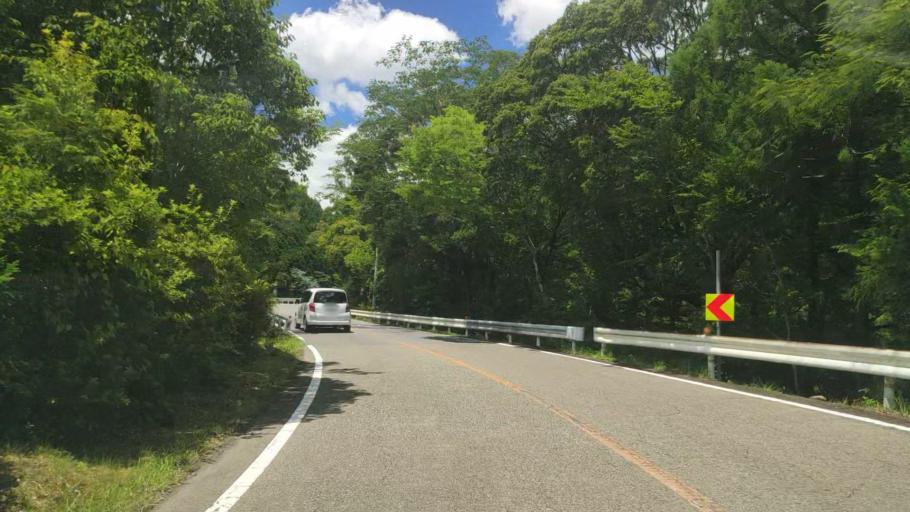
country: JP
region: Mie
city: Owase
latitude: 33.9961
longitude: 136.0253
